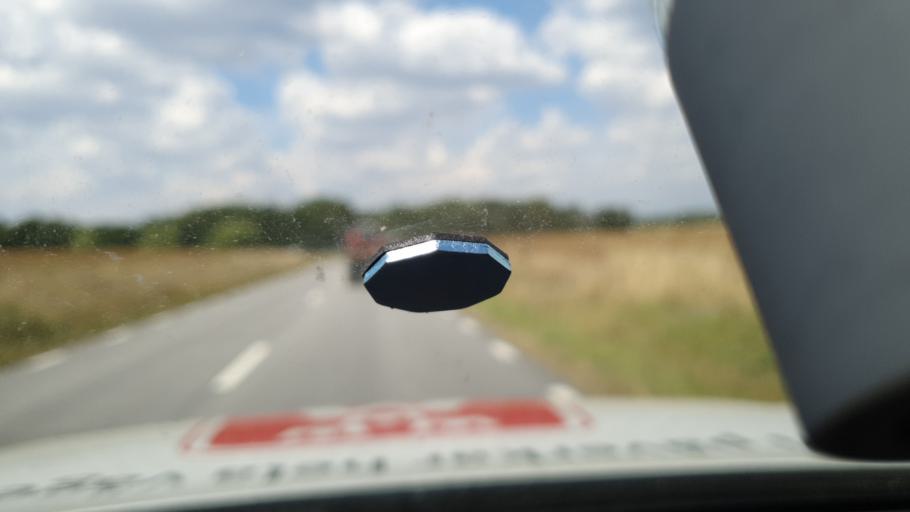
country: SE
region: Skane
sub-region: Sjobo Kommun
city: Blentarp
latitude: 55.5832
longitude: 13.6074
